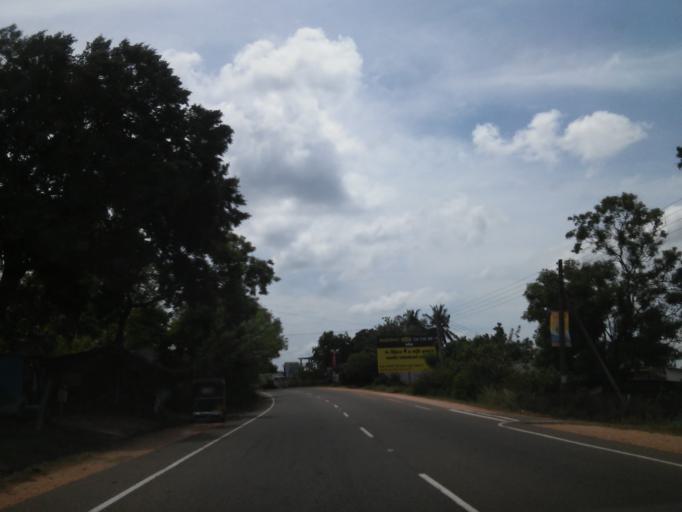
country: LK
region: Eastern Province
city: Trincomalee
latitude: 8.3394
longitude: 80.9781
